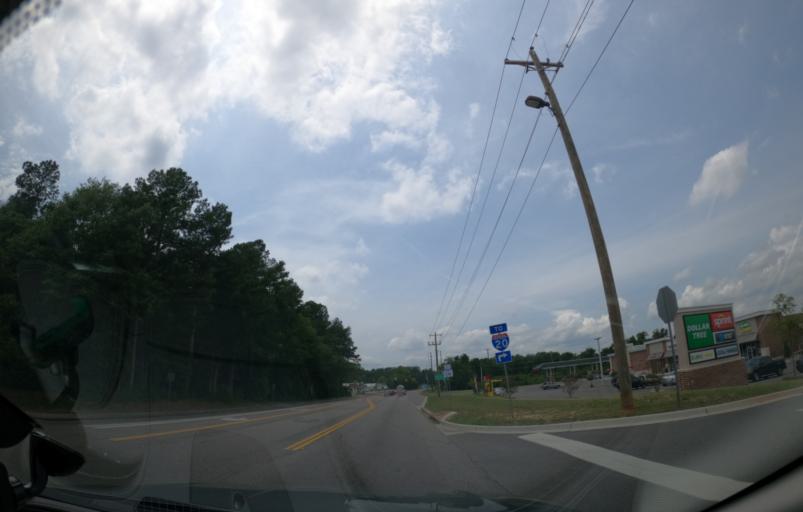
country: US
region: South Carolina
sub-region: Aiken County
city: Aiken
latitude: 33.5801
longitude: -81.7184
